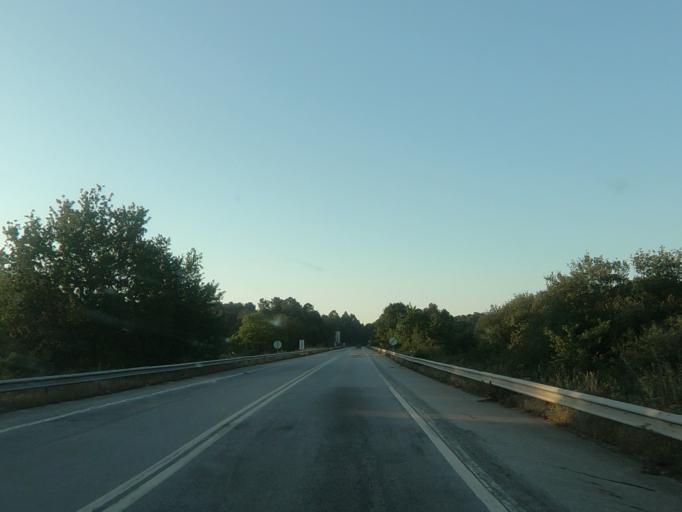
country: PT
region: Viseu
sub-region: Viseu
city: Rio de Loba
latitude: 40.6603
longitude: -7.8627
